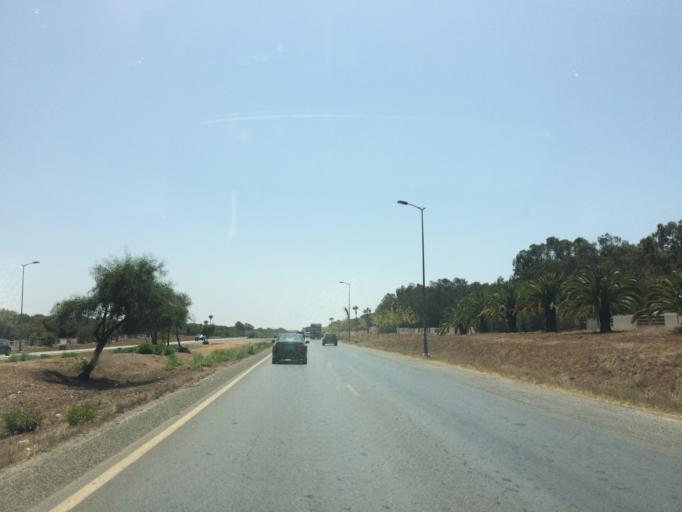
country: MA
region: Rabat-Sale-Zemmour-Zaer
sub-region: Skhirate-Temara
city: Temara
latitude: 33.9598
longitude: -6.9079
